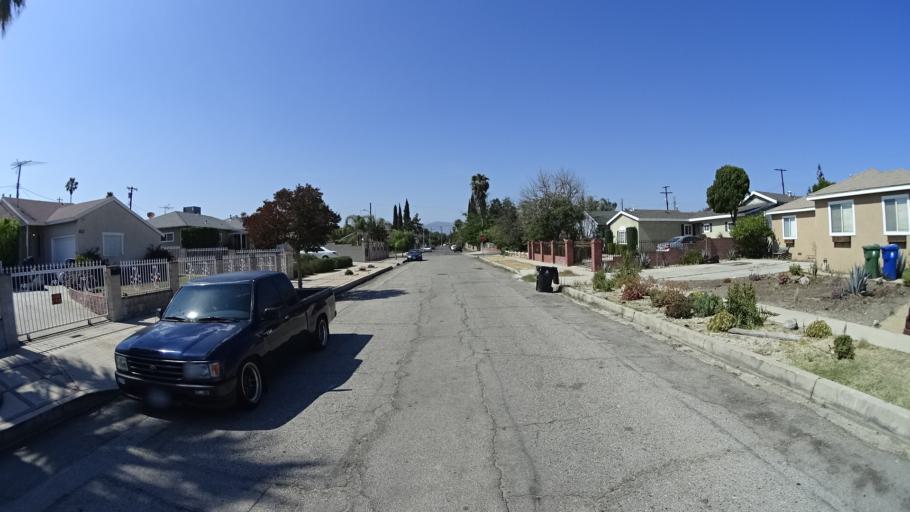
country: US
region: California
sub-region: Los Angeles County
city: Van Nuys
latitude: 34.2174
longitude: -118.4155
